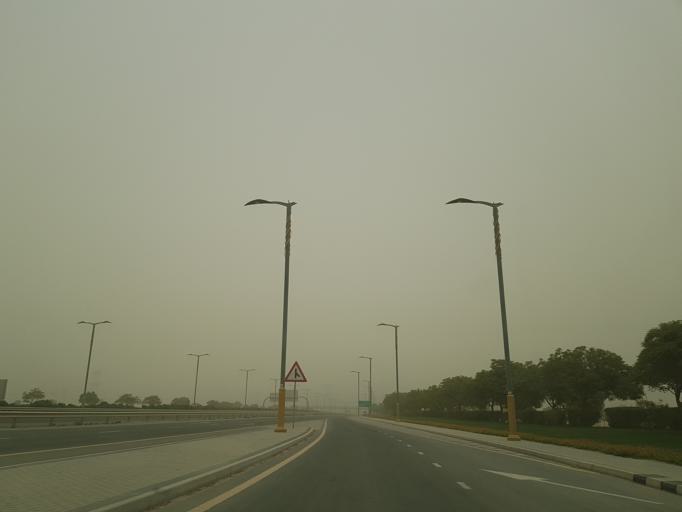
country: AE
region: Dubai
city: Dubai
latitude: 25.1626
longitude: 55.2987
